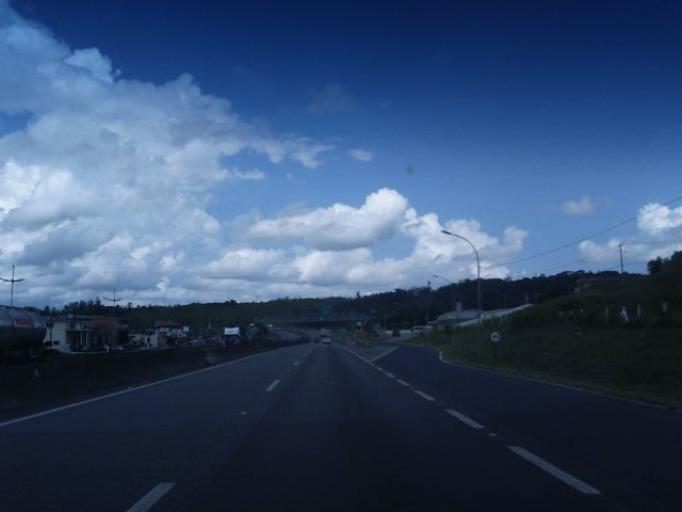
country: BR
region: Sao Paulo
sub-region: Cajati
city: Cajati
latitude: -24.7304
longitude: -48.1042
